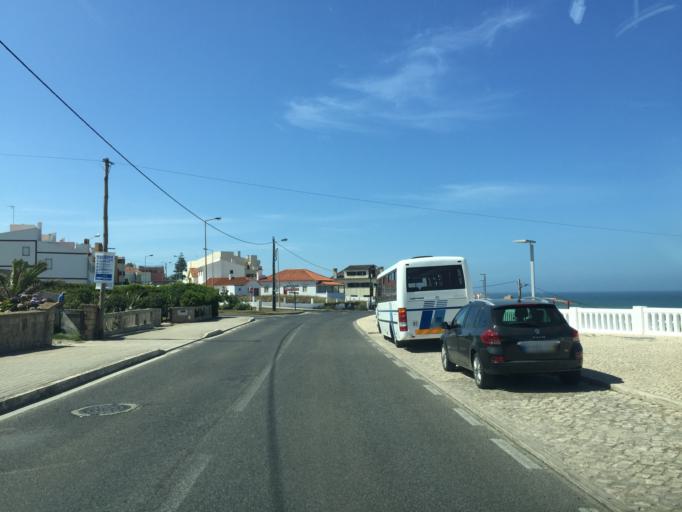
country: PT
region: Lisbon
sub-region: Torres Vedras
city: Silveira
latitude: 39.1398
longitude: -9.3775
